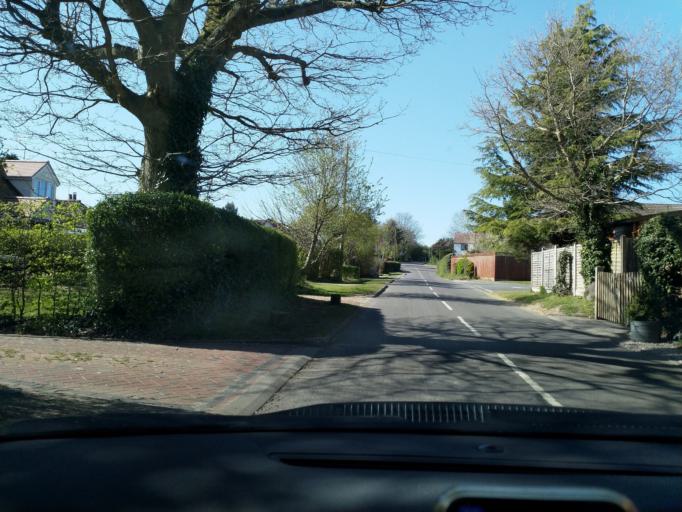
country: GB
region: England
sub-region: Warwickshire
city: Wroxall
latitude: 52.2933
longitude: -1.6726
